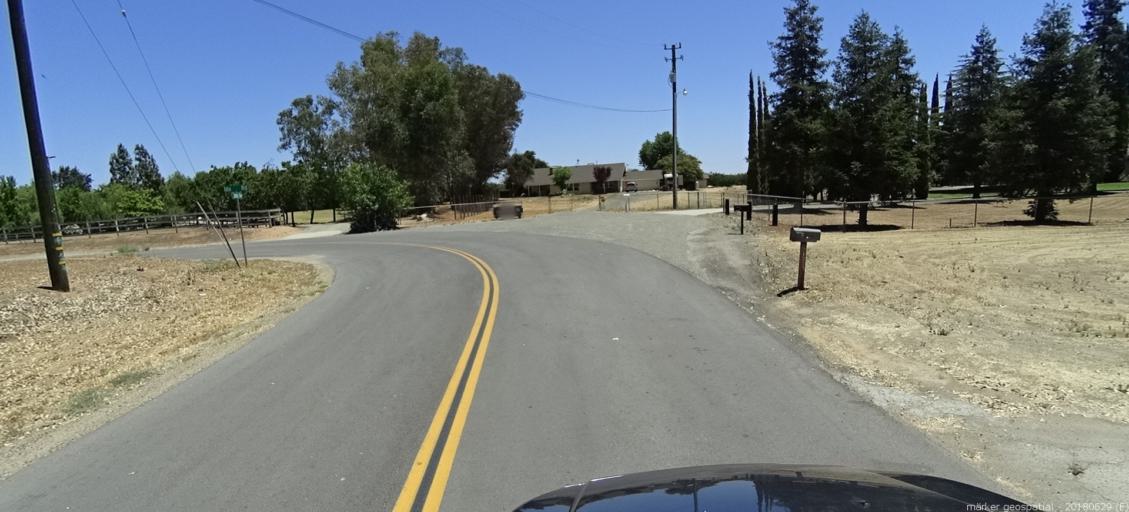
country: US
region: California
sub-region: Madera County
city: Parksdale
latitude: 36.9900
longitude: -119.9765
